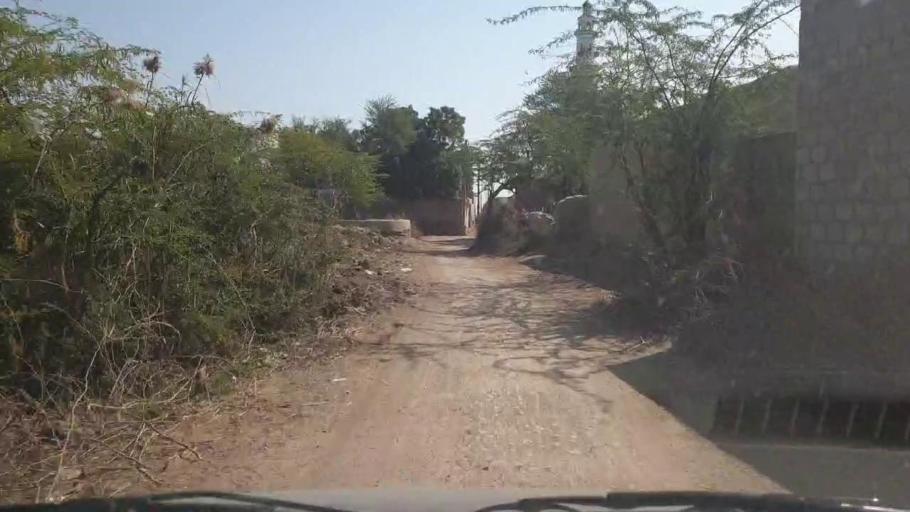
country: PK
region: Sindh
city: Samaro
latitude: 25.2637
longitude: 69.3443
